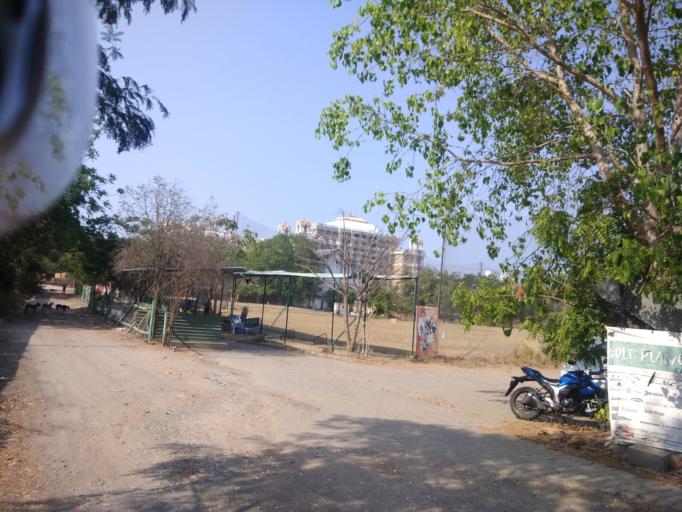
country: IN
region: Tamil Nadu
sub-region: Kancheepuram
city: Alandur
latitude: 13.0084
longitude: 80.2182
